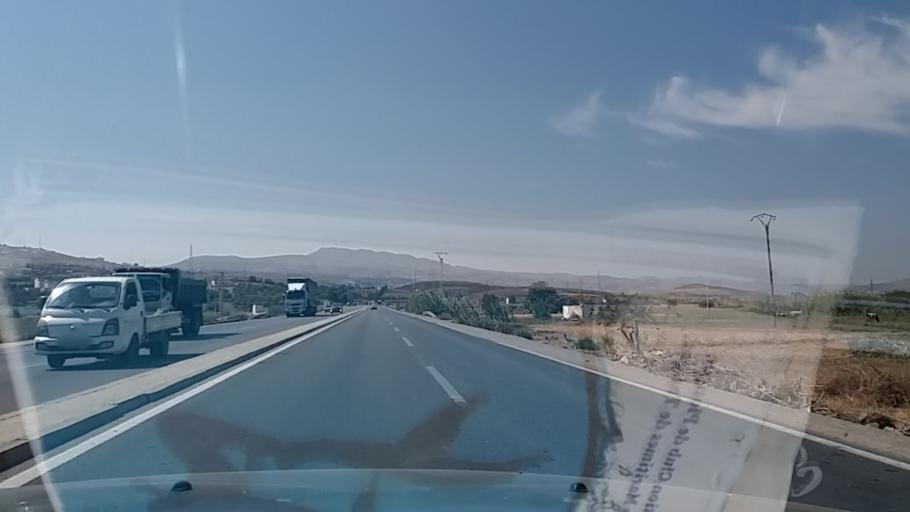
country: MA
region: Tanger-Tetouan
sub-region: Tetouan
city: Saddina
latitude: 35.5594
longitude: -5.4621
